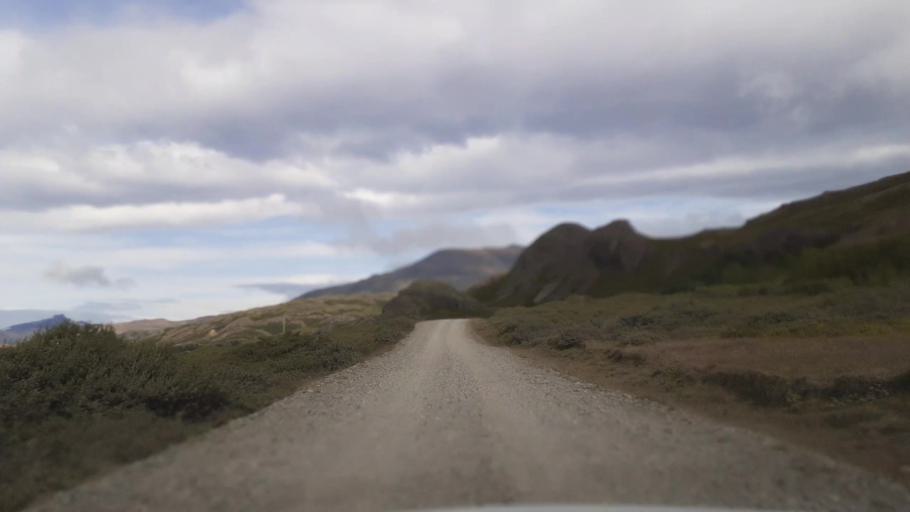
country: IS
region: East
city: Hoefn
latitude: 64.4279
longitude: -14.8849
